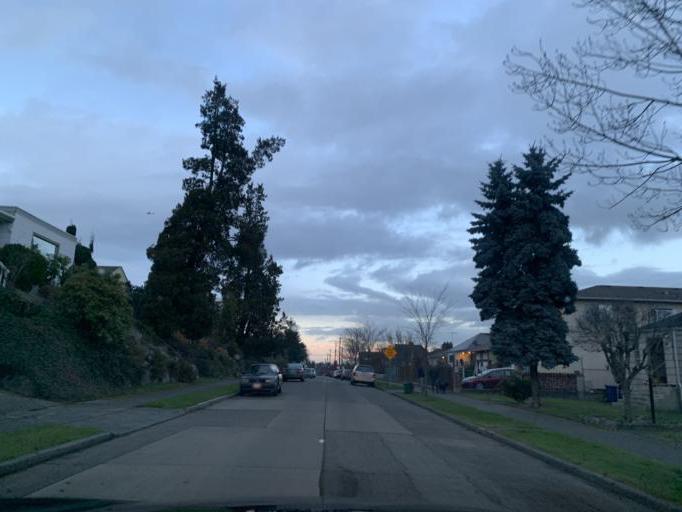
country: US
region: Washington
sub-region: King County
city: Seattle
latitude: 47.5657
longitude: -122.3147
